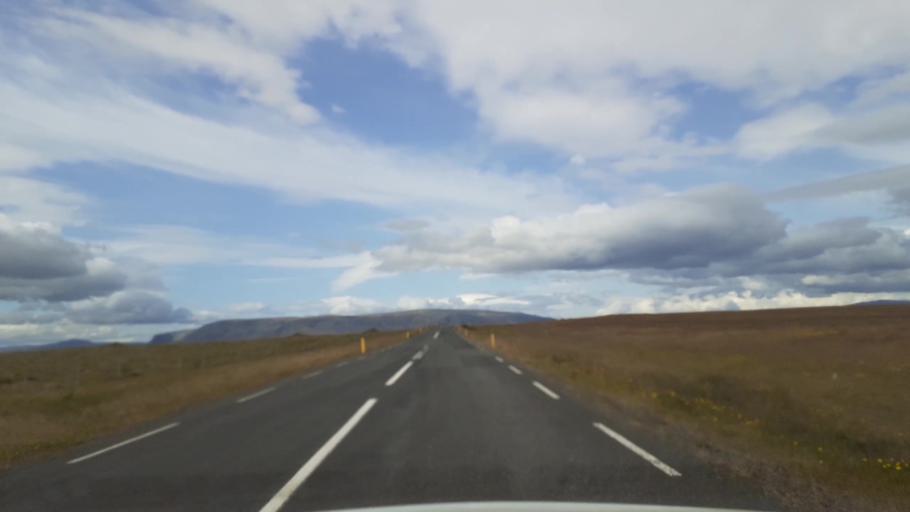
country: IS
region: South
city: Selfoss
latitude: 63.9183
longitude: -20.8463
